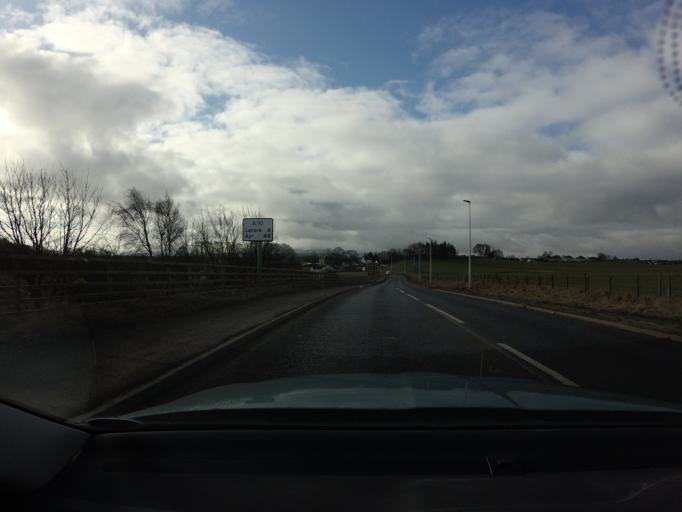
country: GB
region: Scotland
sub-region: South Lanarkshire
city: Carnwath
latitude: 55.7004
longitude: -3.6897
